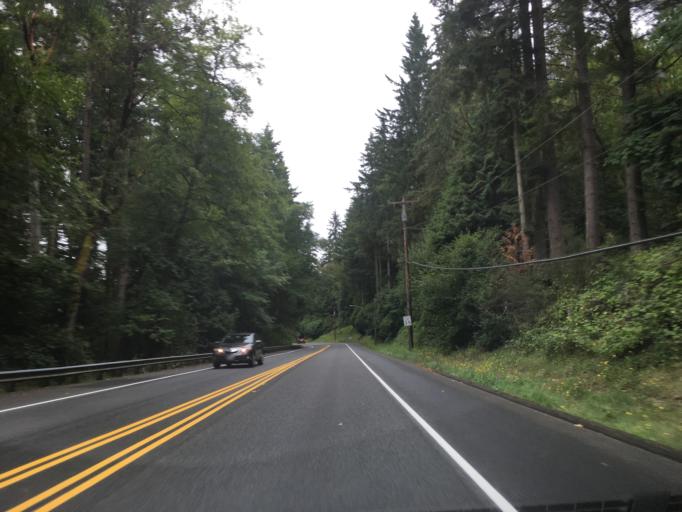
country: US
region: Washington
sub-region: King County
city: Inglewood-Finn Hill
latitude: 47.7239
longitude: -122.2406
